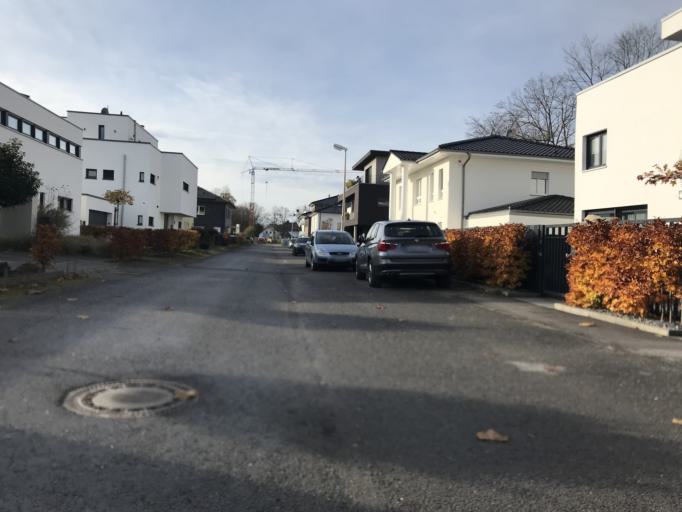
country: DE
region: North Rhine-Westphalia
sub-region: Regierungsbezirk Arnsberg
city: Hamm
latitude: 51.6860
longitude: 7.8386
